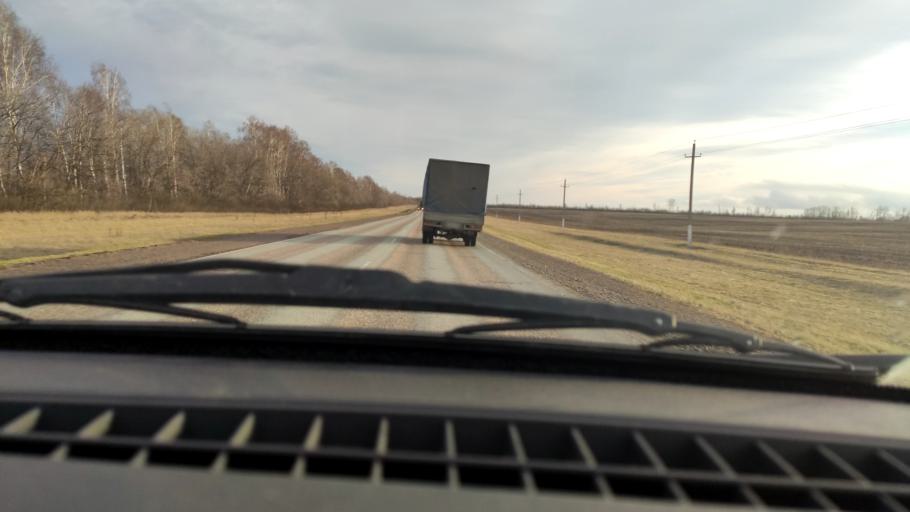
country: RU
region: Bashkortostan
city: Davlekanovo
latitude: 54.3373
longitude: 55.1703
